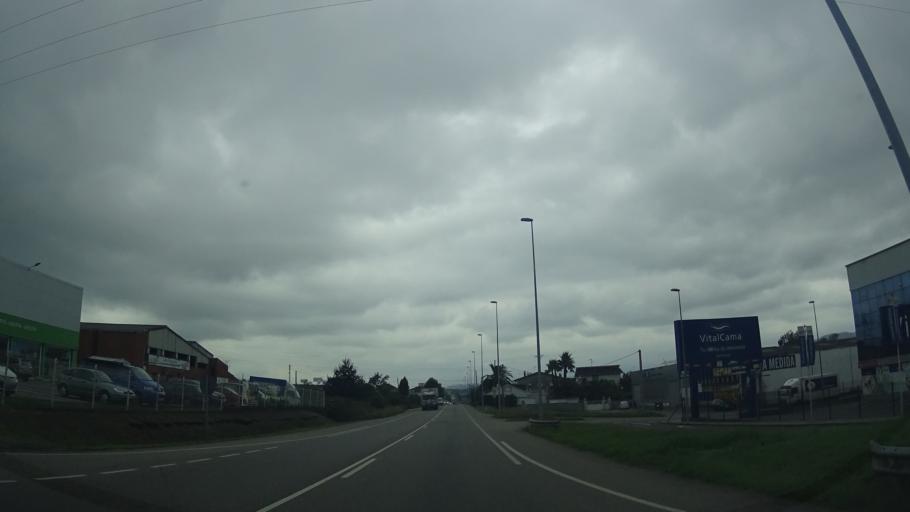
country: ES
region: Asturias
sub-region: Province of Asturias
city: Lugones
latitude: 43.3837
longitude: -5.7656
